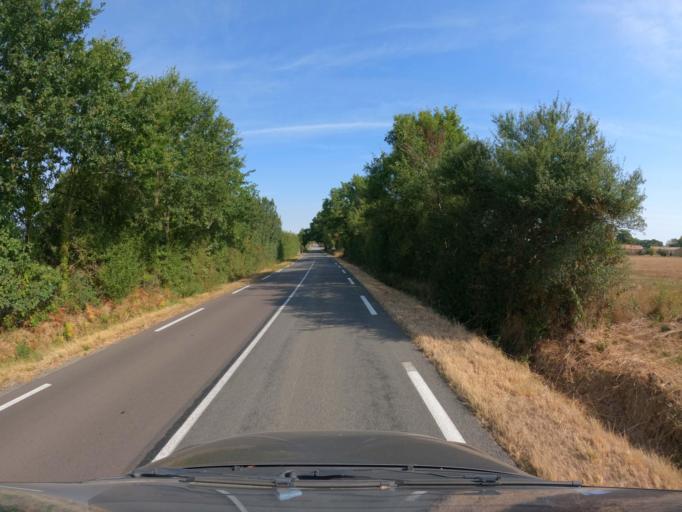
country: FR
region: Pays de la Loire
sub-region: Departement de la Vendee
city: Falleron
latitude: 46.8751
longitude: -1.7034
